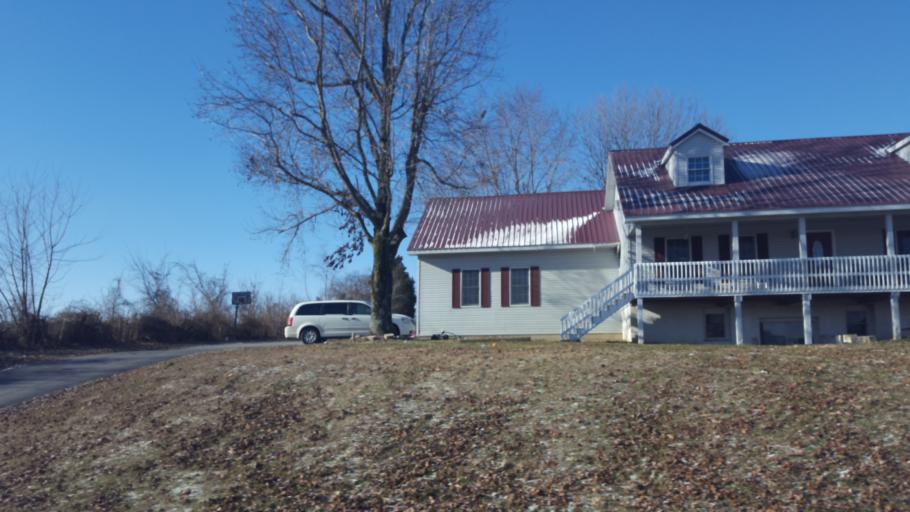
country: US
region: Kentucky
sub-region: Crittenden County
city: Marion
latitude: 37.4256
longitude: -88.0449
